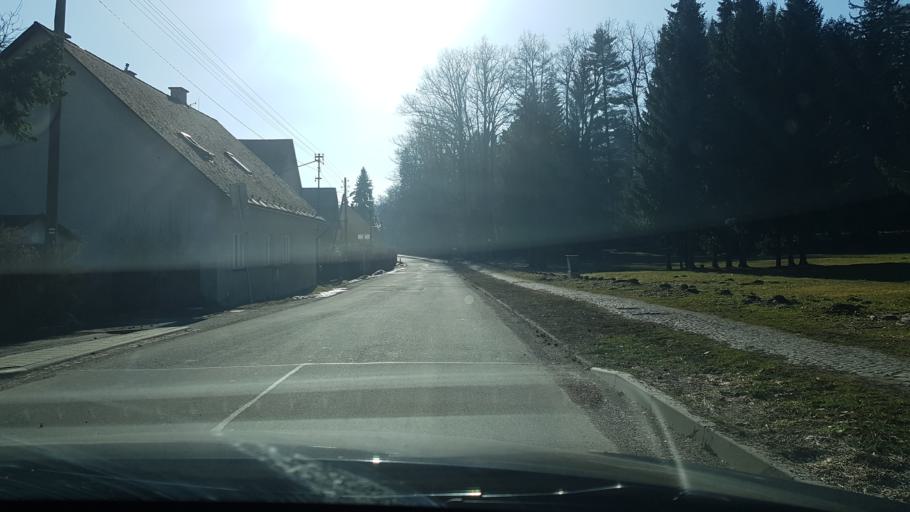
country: CZ
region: Olomoucky
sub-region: Okres Sumperk
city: Velke Losiny
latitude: 50.0349
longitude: 17.0404
